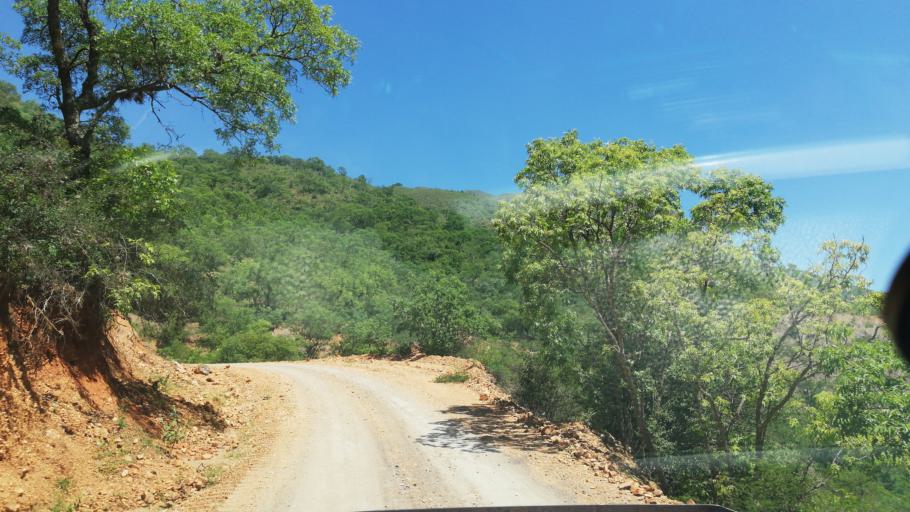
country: BO
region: Cochabamba
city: Mizque
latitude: -17.8773
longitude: -65.2909
